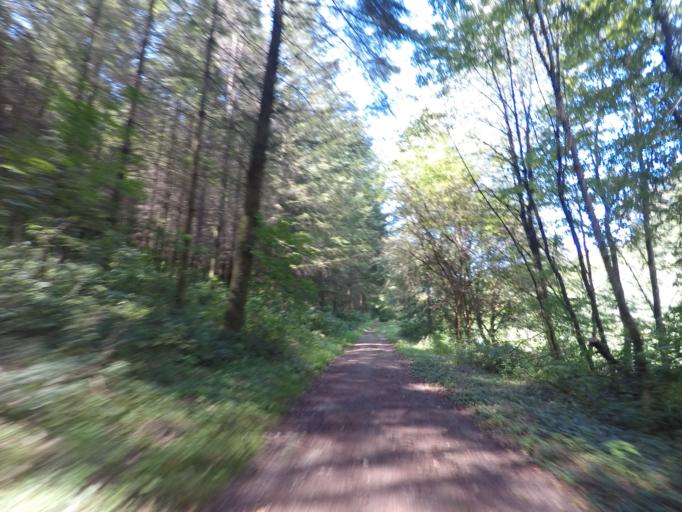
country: LU
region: Luxembourg
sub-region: Canton de Luxembourg
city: Strassen
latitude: 49.6296
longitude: 6.0933
